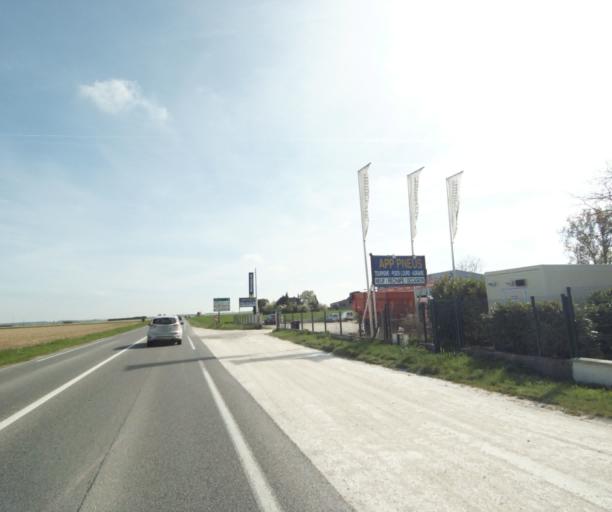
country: FR
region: Ile-de-France
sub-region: Departement de Seine-et-Marne
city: Nangis
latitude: 48.5630
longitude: 3.0359
